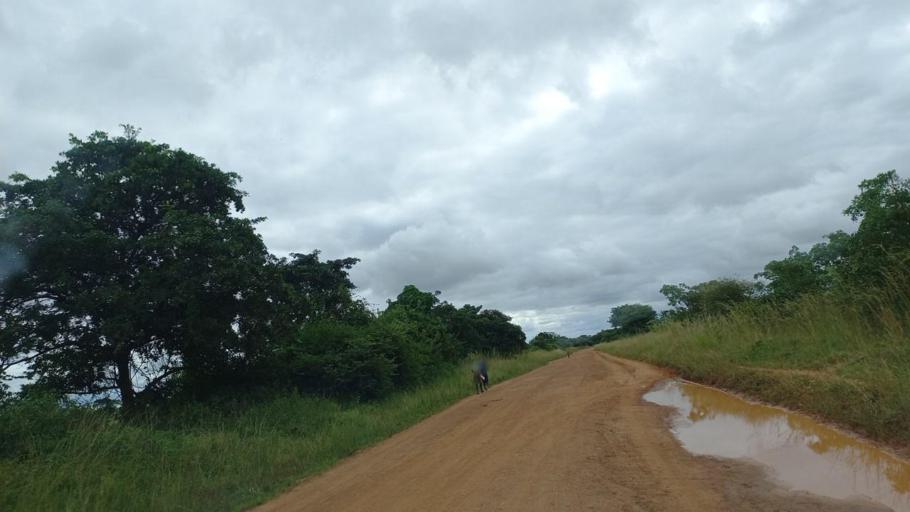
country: ZM
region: Lusaka
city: Chongwe
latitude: -15.4563
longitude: 28.8696
